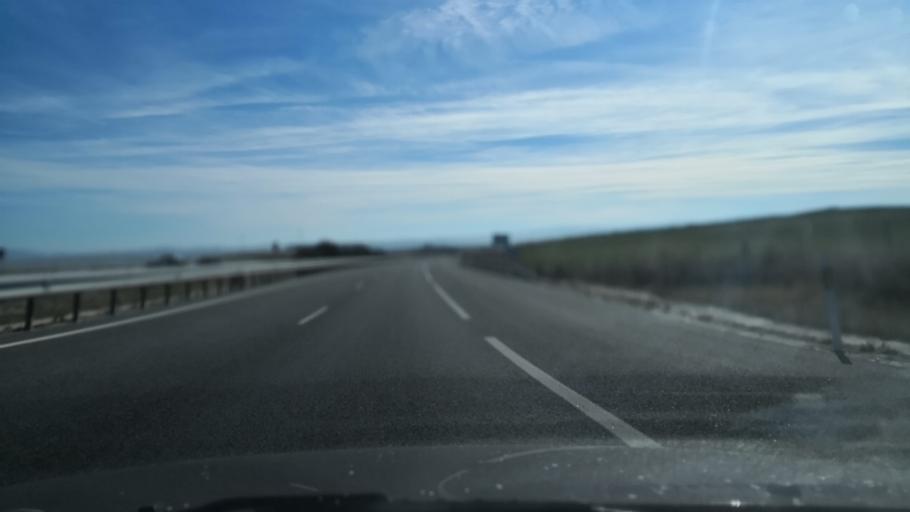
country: ES
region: Castille and Leon
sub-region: Provincia de Avila
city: Munogrande
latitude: 40.8314
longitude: -4.9402
